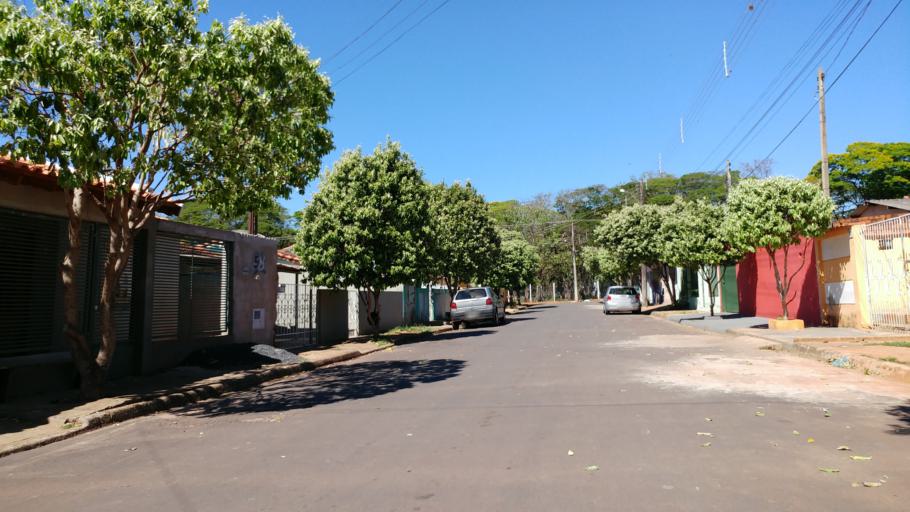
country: BR
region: Sao Paulo
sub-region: Paraguacu Paulista
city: Paraguacu Paulista
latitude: -22.4205
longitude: -50.5685
